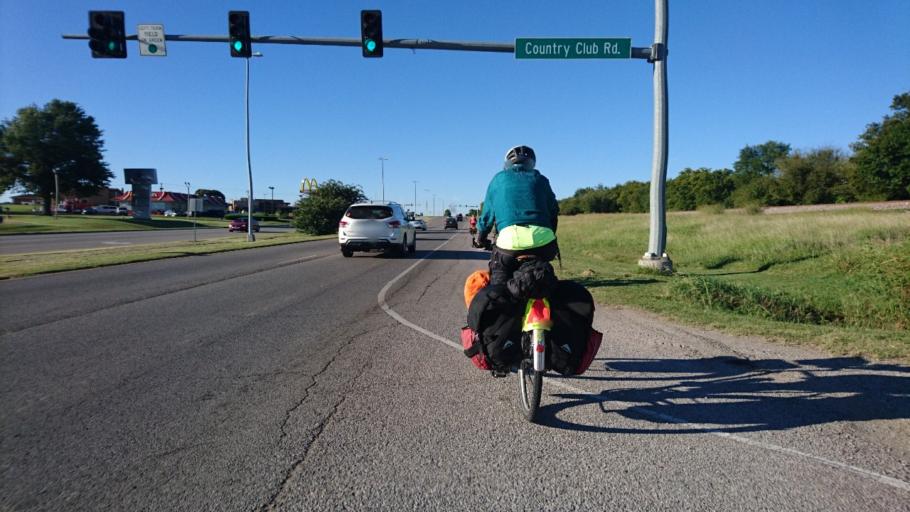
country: US
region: Oklahoma
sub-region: Rogers County
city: Claremore
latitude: 36.2930
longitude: -95.6311
